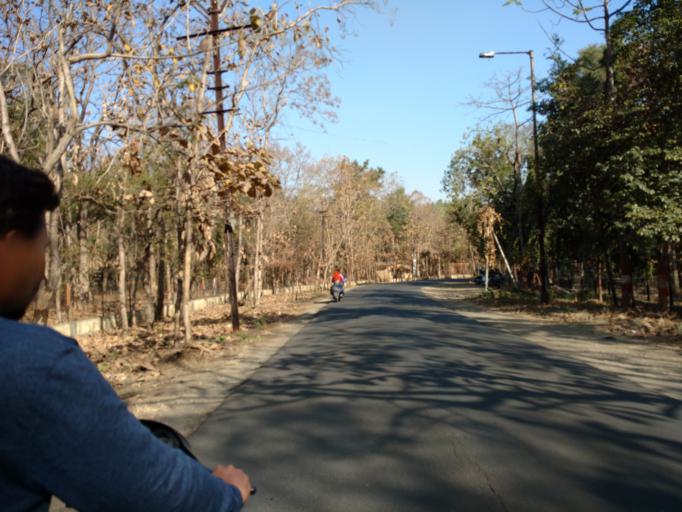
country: IN
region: Maharashtra
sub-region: Nagpur Division
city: Nagpur
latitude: 21.1688
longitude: 79.0589
